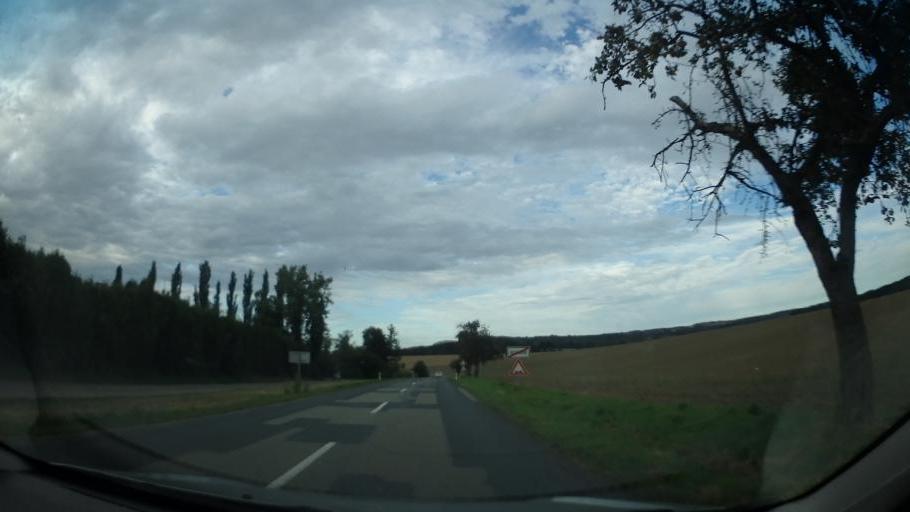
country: CZ
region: South Moravian
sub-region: Okres Blansko
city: Boskovice
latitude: 49.4992
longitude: 16.6660
